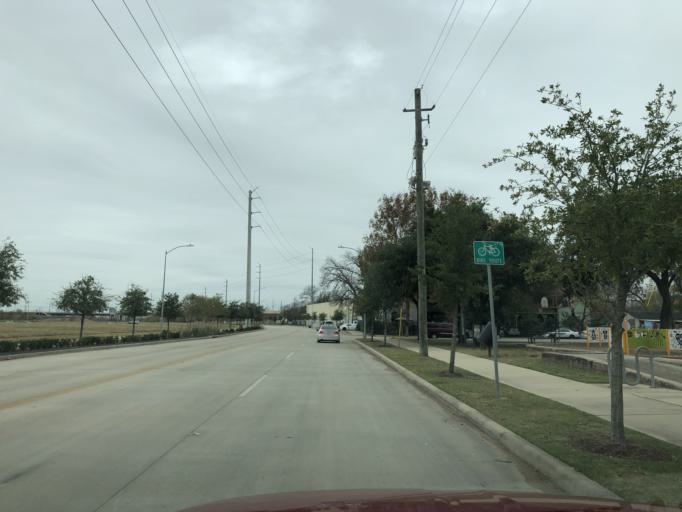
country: US
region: Texas
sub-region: Harris County
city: Houston
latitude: 29.7745
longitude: -95.3523
